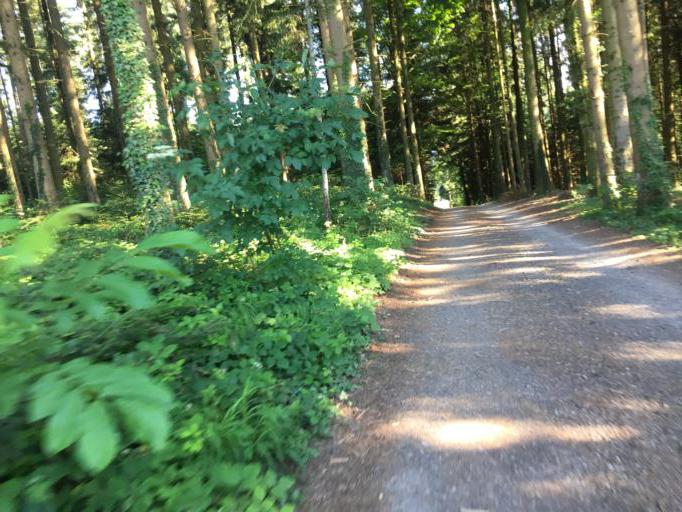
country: CH
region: Bern
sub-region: Bern-Mittelland District
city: Niederwichtrach
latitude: 46.8595
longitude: 7.5870
